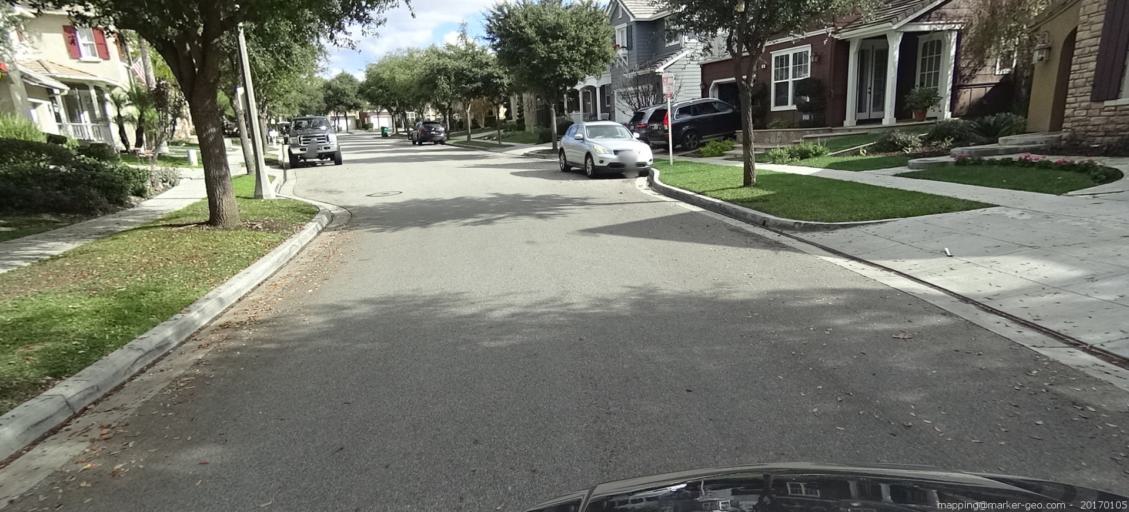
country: US
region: California
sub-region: Orange County
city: Ladera Ranch
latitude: 33.5662
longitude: -117.6375
